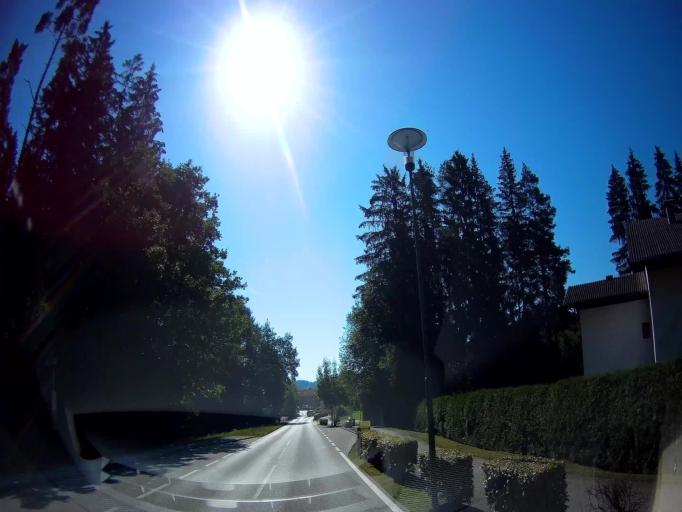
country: AT
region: Carinthia
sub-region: Politischer Bezirk Volkermarkt
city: Eberndorf
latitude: 46.6110
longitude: 14.5954
